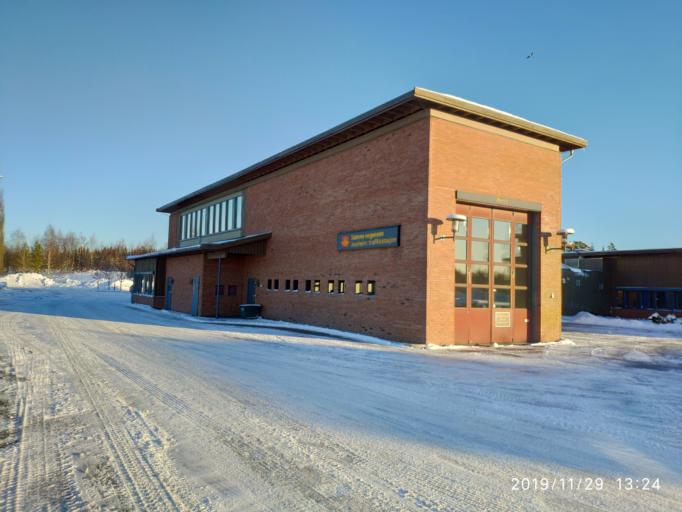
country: NO
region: Akershus
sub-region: Ullensaker
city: Jessheim
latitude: 60.1676
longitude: 11.1588
